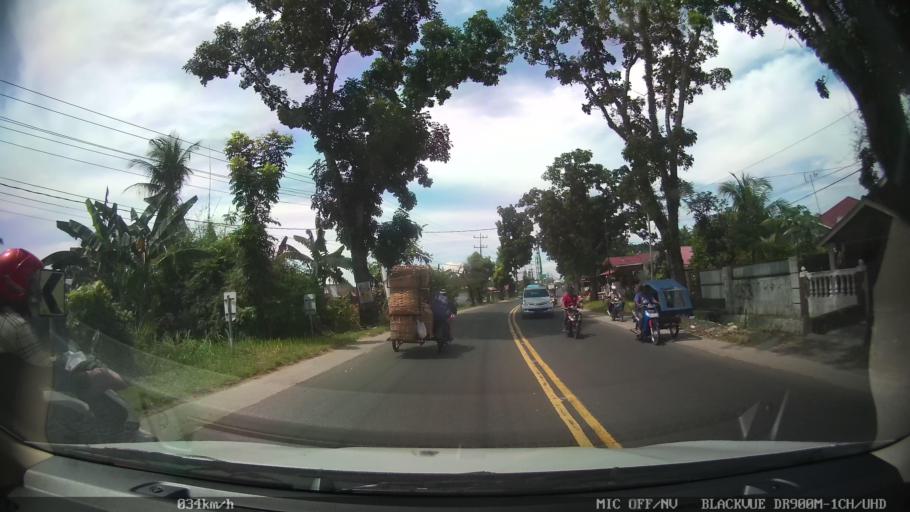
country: ID
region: North Sumatra
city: Binjai
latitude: 3.6306
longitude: 98.5106
